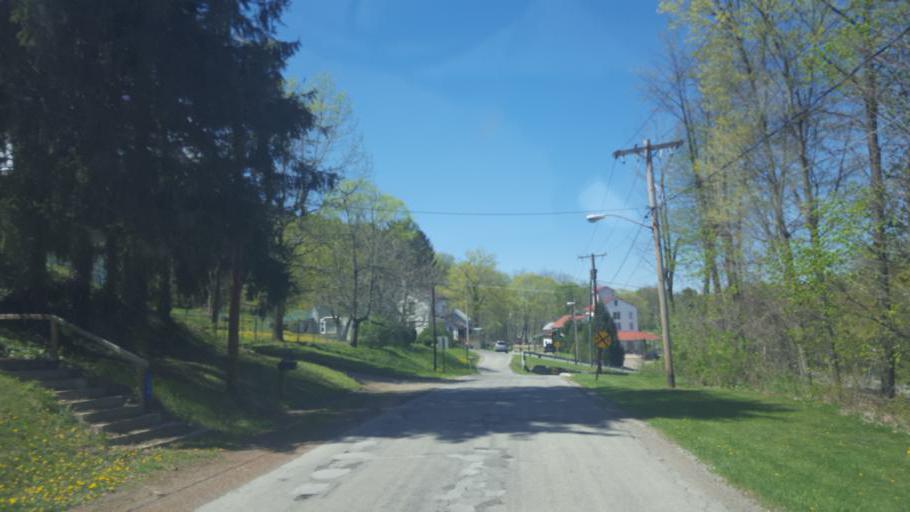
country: US
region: Ohio
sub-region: Richland County
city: Lincoln Heights
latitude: 40.7016
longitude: -82.4183
